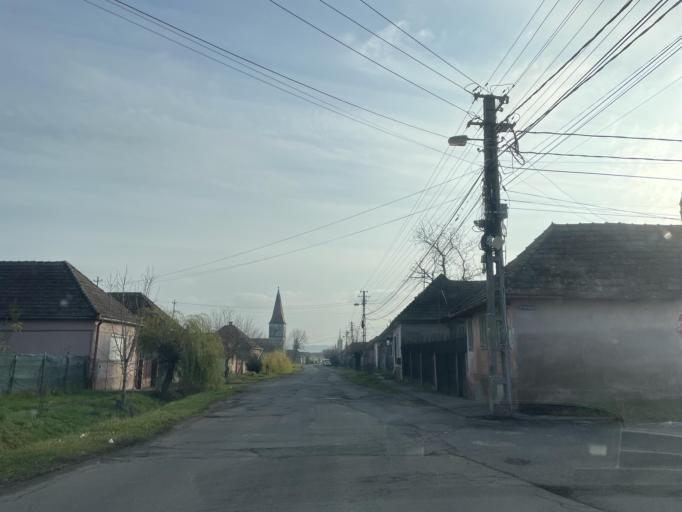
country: RO
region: Mures
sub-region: Municipiul Reghin
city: Apalina
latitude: 46.7515
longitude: 24.6932
